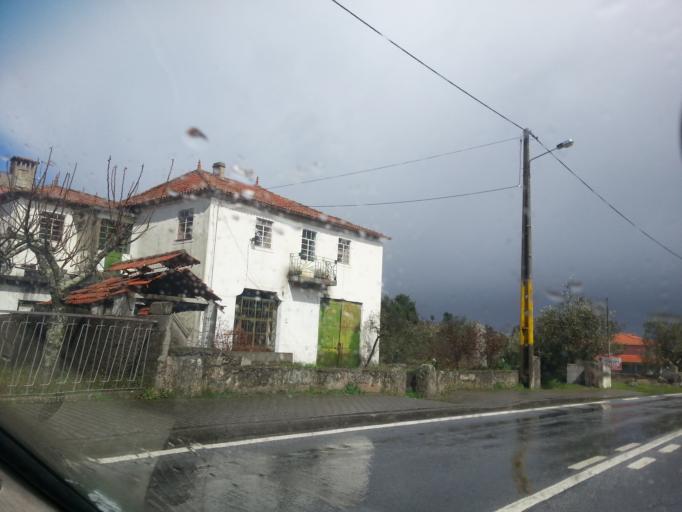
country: PT
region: Guarda
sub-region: Fornos de Algodres
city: Fornos de Algodres
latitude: 40.5600
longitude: -7.4835
